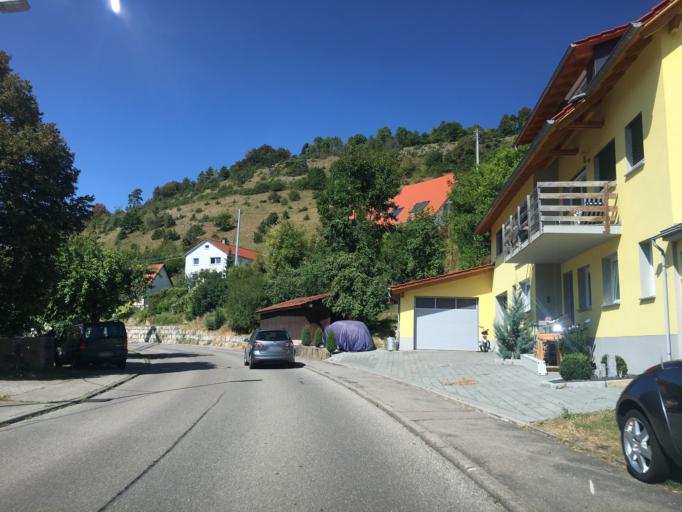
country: DE
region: Baden-Wuerttemberg
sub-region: Tuebingen Region
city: Munsingen
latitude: 48.3448
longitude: 9.4879
